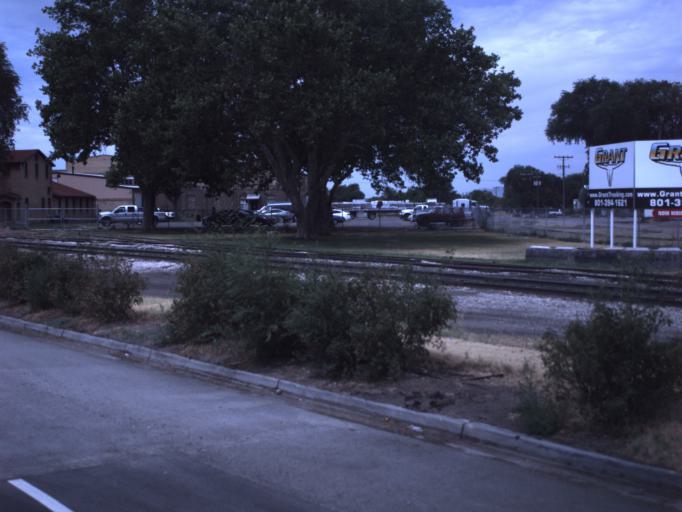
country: US
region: Utah
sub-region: Weber County
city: Ogden
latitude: 41.2230
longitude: -112.0008
